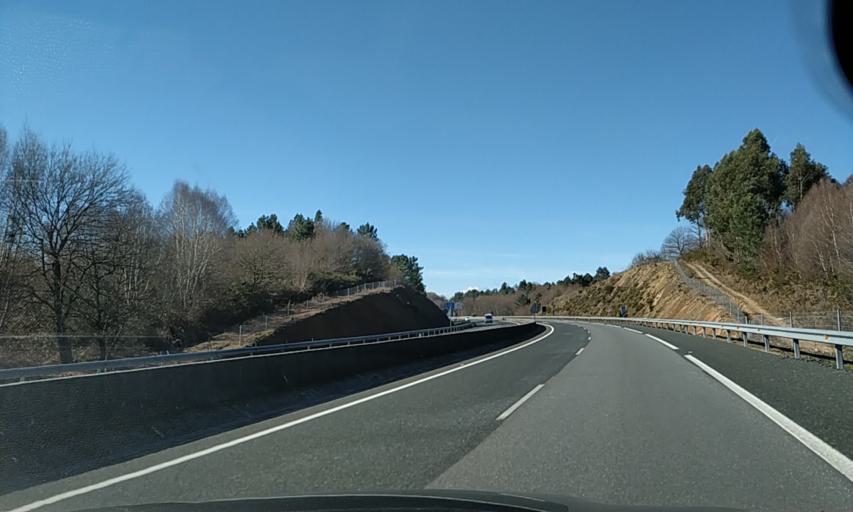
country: ES
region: Galicia
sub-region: Provincia de Pontevedra
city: Lalin
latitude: 42.6699
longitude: -8.1507
